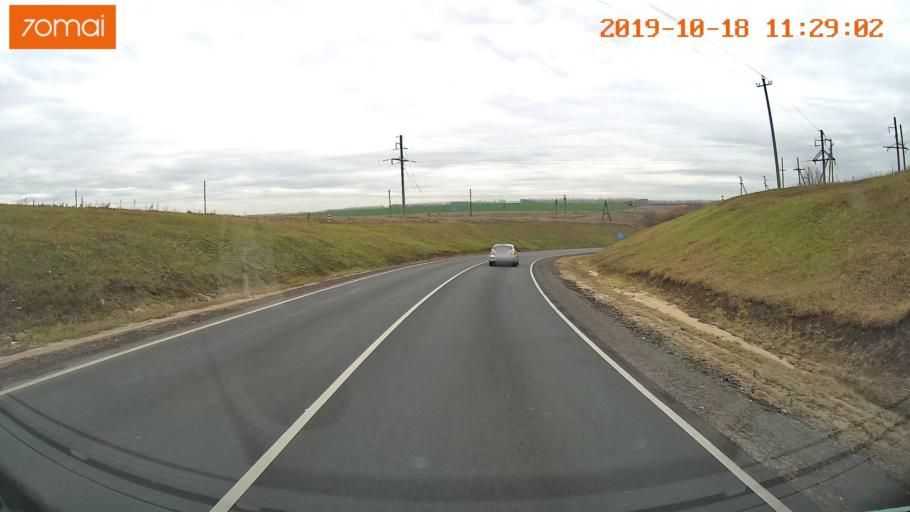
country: RU
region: Tula
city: Kimovsk
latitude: 54.1579
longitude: 38.6704
